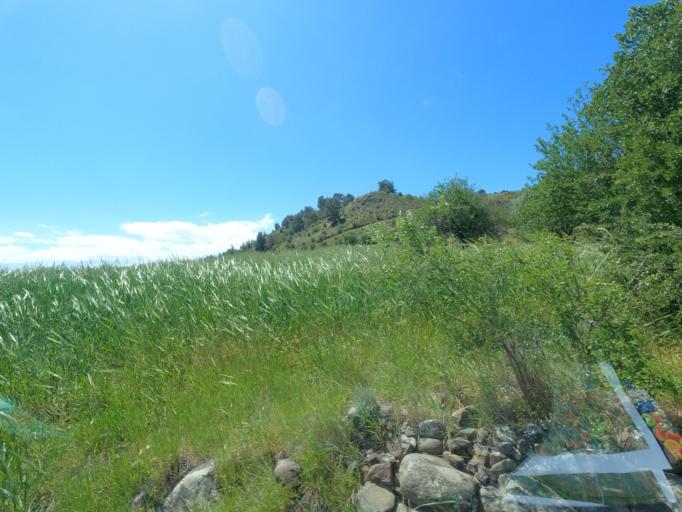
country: CY
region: Lefkosia
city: Peristerona
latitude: 35.0478
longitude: 33.0771
